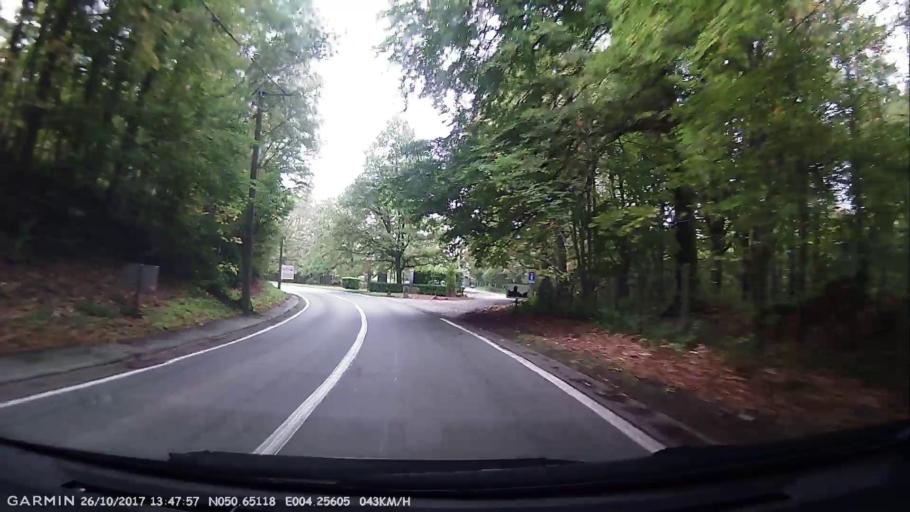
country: BE
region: Wallonia
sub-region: Province du Brabant Wallon
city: Ittre
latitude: 50.6511
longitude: 4.2560
